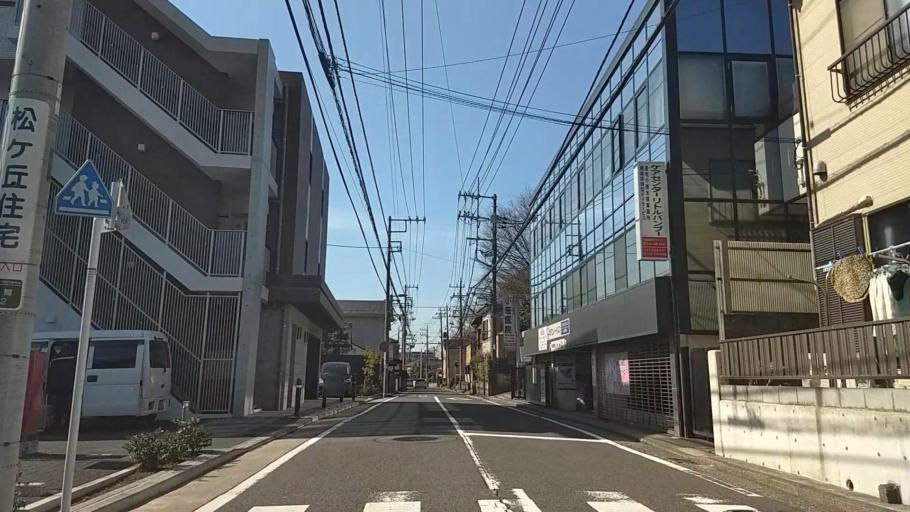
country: JP
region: Kanagawa
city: Kamakura
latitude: 35.3588
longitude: 139.5391
